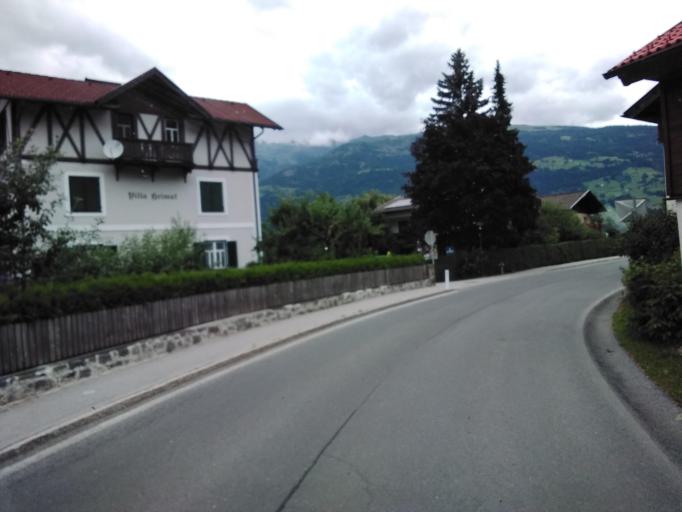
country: AT
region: Tyrol
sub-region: Politischer Bezirk Lienz
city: Amlach
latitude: 46.8143
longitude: 12.7618
